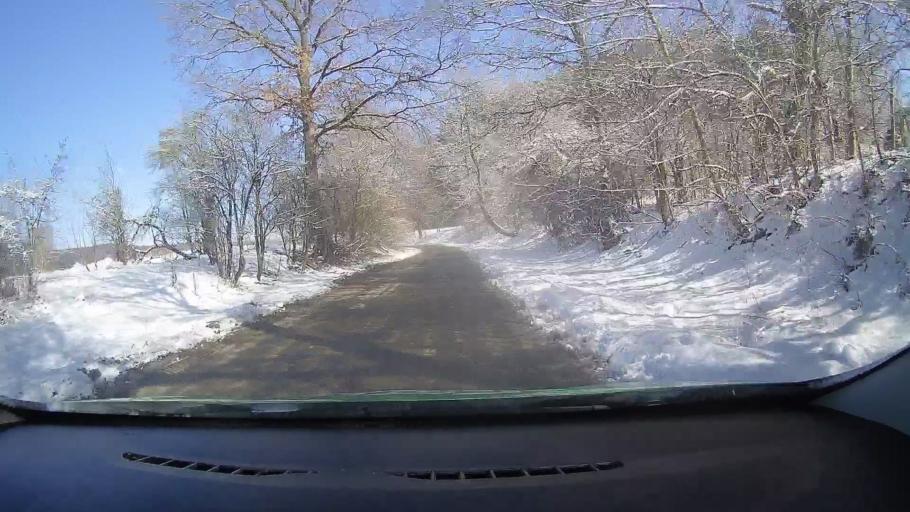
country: RO
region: Sibiu
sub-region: Comuna Mosna
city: Mosna
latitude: 46.0170
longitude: 24.4084
